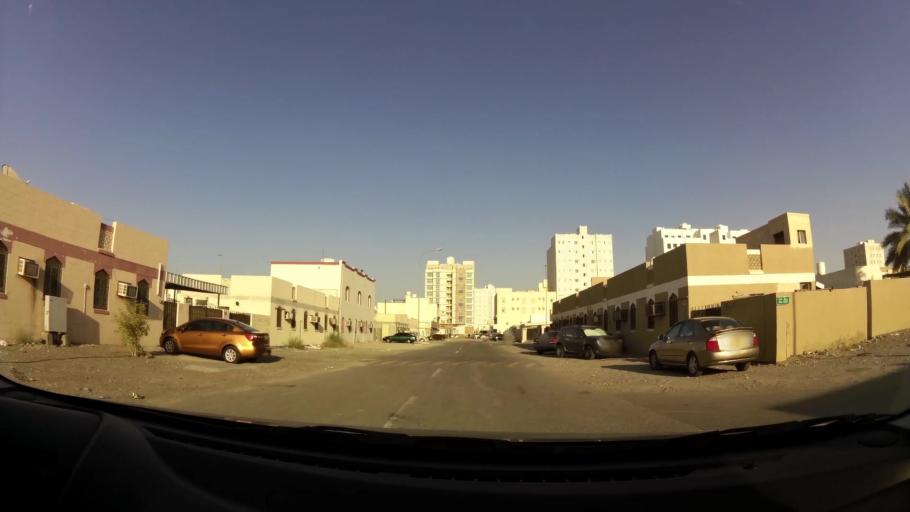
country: OM
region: Muhafazat Masqat
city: As Sib al Jadidah
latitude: 23.6279
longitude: 58.1938
